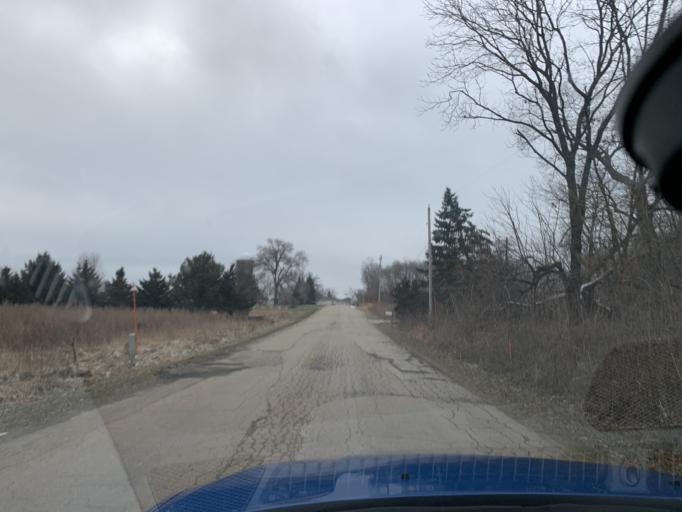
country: US
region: Wisconsin
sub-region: Dane County
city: Middleton
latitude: 43.0735
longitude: -89.5633
